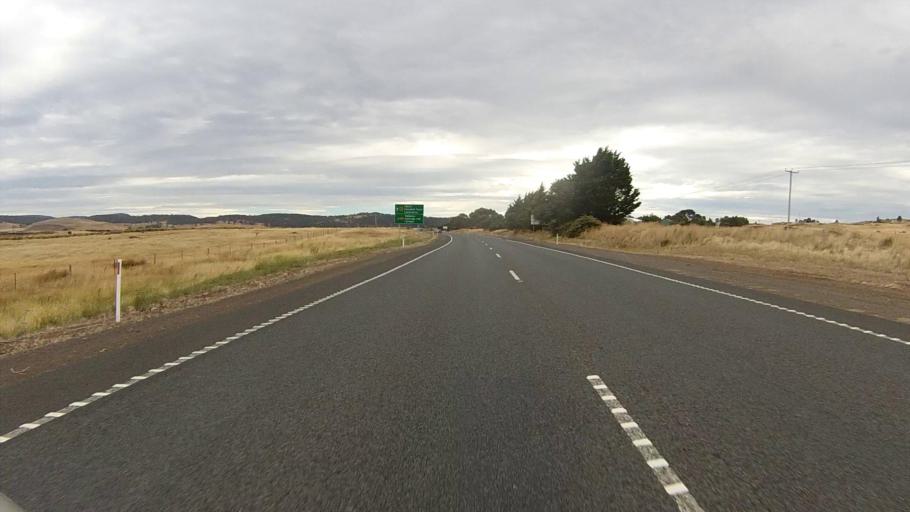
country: AU
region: Tasmania
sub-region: Brighton
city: Bridgewater
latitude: -42.3156
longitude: 147.3541
